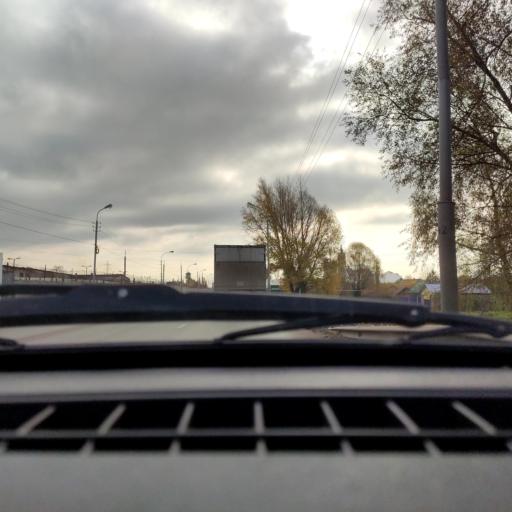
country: RU
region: Bashkortostan
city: Iglino
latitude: 54.7848
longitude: 56.2210
